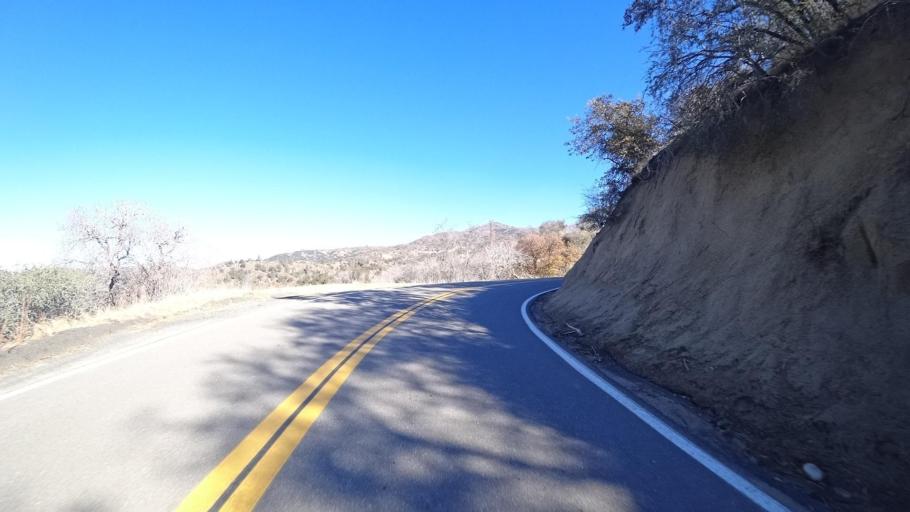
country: US
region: California
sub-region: Kern County
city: Alta Sierra
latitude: 35.7370
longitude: -118.6442
